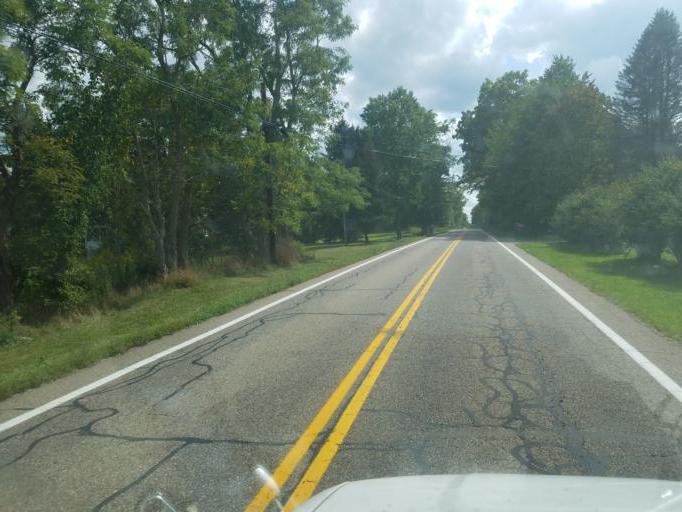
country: US
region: Ohio
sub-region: Portage County
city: Hiram
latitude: 41.3380
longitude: -81.1432
